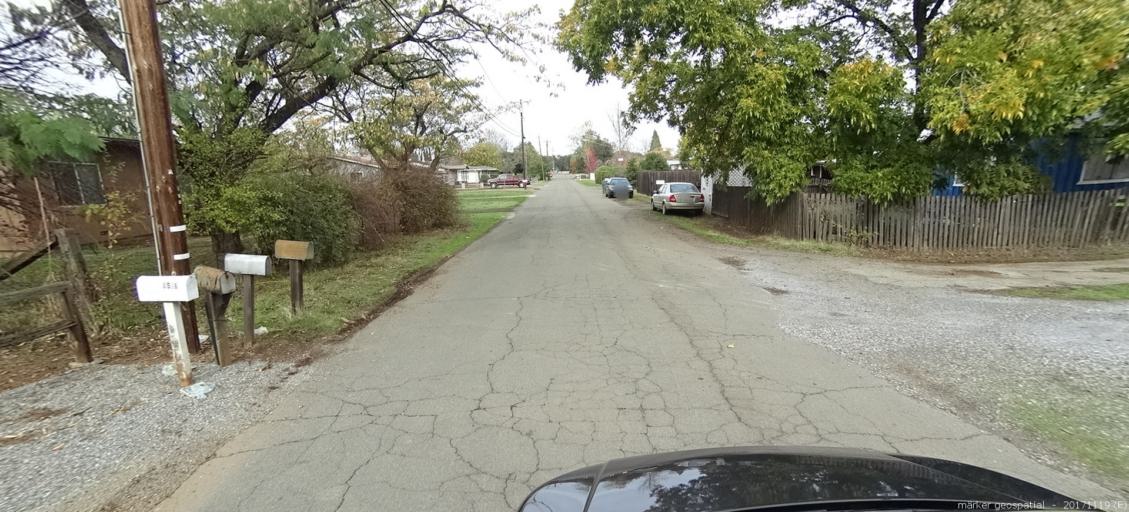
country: US
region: California
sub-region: Shasta County
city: Anderson
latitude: 40.4777
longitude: -122.2670
